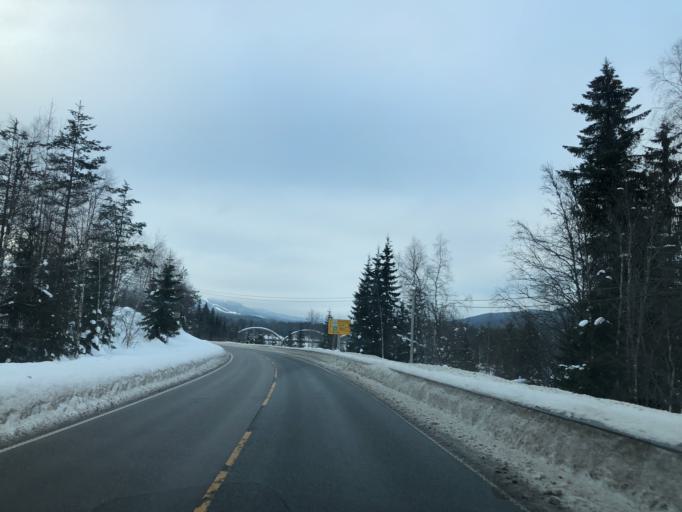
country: NO
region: Hedmark
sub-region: Trysil
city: Innbygda
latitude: 61.2685
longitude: 12.3051
